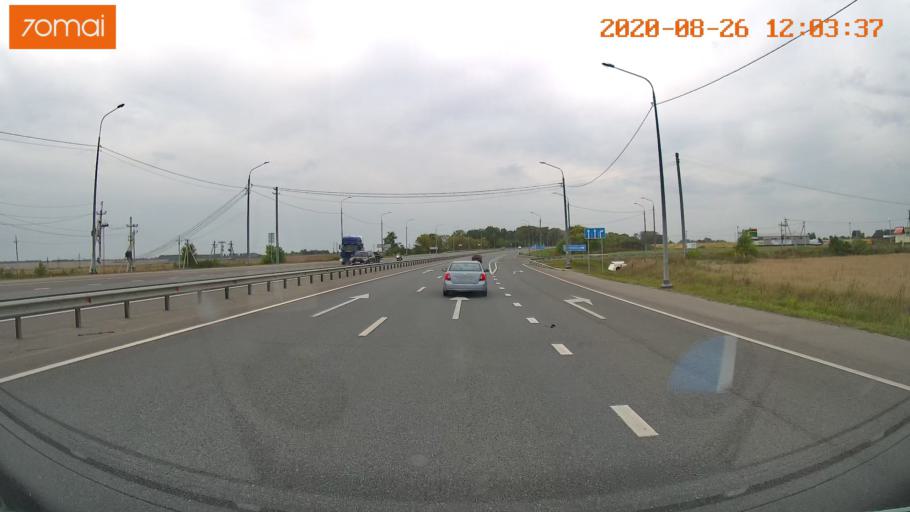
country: RU
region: Rjazan
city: Kiritsy
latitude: 54.3019
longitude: 40.2030
